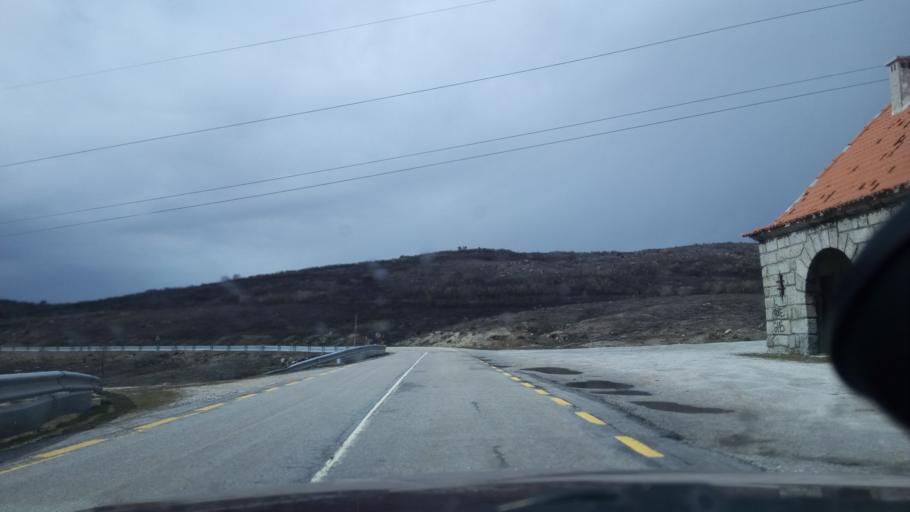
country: PT
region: Guarda
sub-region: Manteigas
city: Manteigas
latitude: 40.4182
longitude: -7.6033
